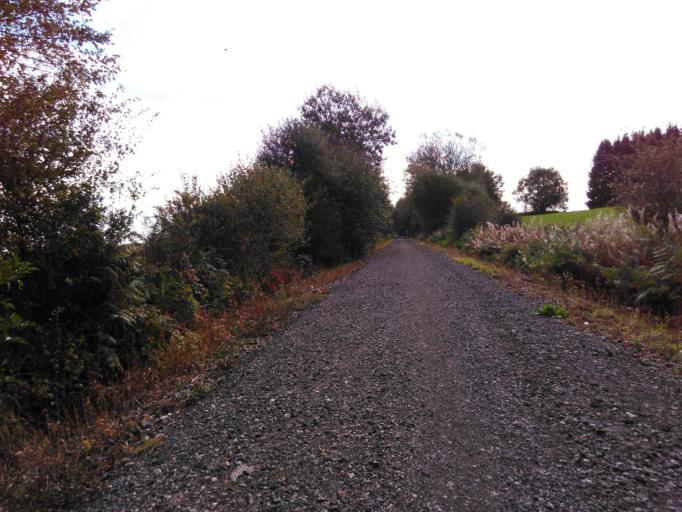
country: BE
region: Wallonia
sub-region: Province du Luxembourg
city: Neufchateau
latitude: 49.9100
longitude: 5.4464
